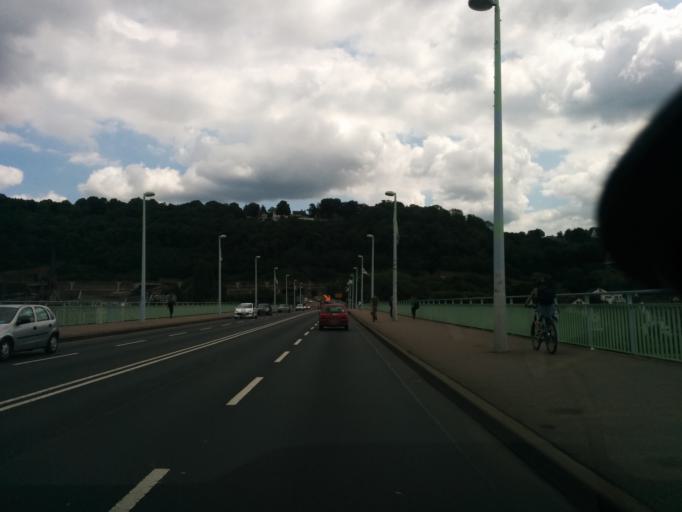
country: DE
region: Rheinland-Pfalz
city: Koblenz
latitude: 50.3533
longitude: 7.6041
